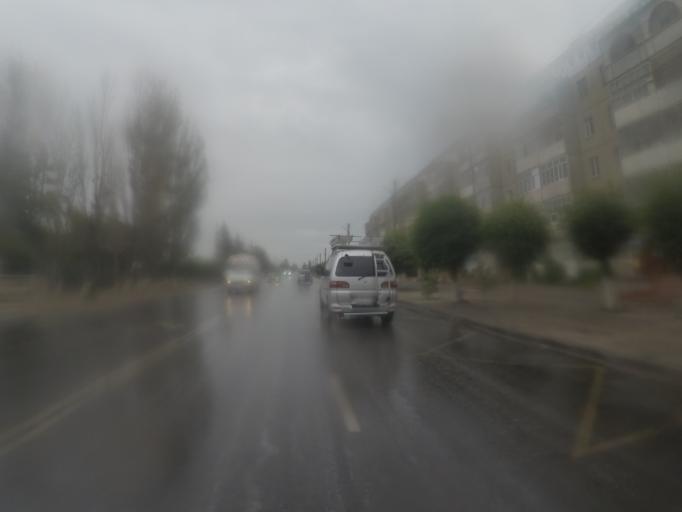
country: KG
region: Ysyk-Koel
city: Balykchy
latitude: 42.4551
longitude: 76.1884
